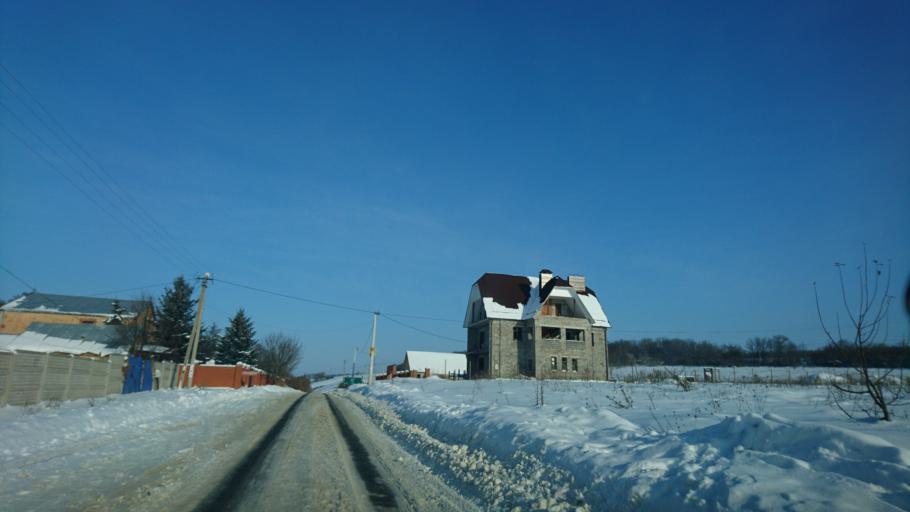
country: RU
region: Belgorod
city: Severnyy
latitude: 50.7240
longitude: 36.6109
